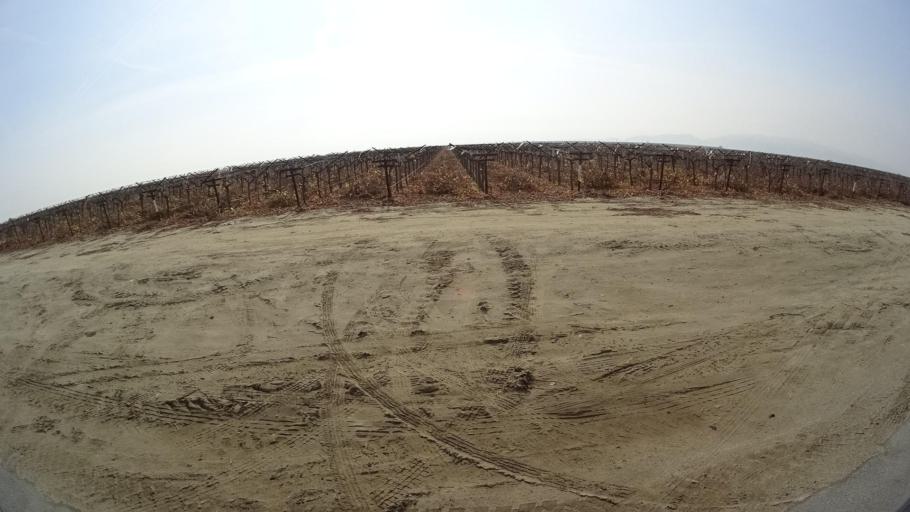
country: US
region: California
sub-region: Kern County
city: Weedpatch
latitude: 35.0744
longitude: -118.9318
